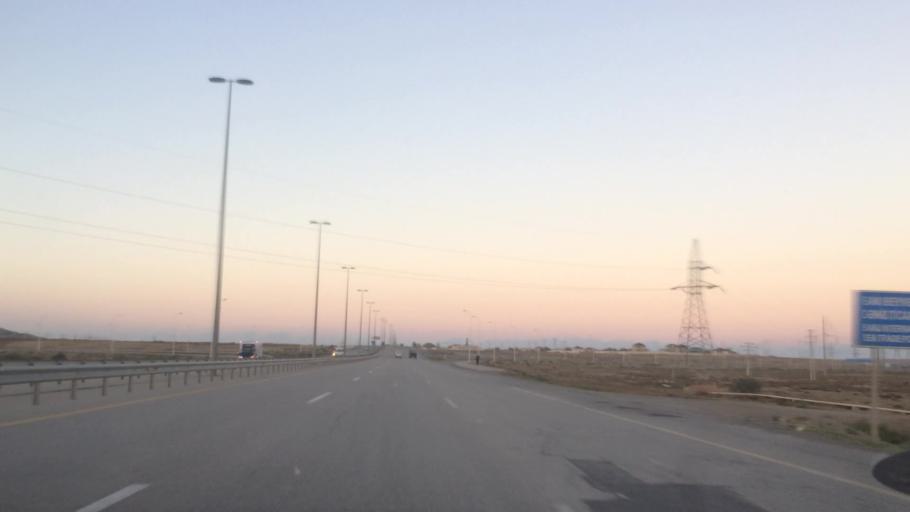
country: AZ
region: Baki
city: Qobustan
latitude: 39.9780
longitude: 49.4207
